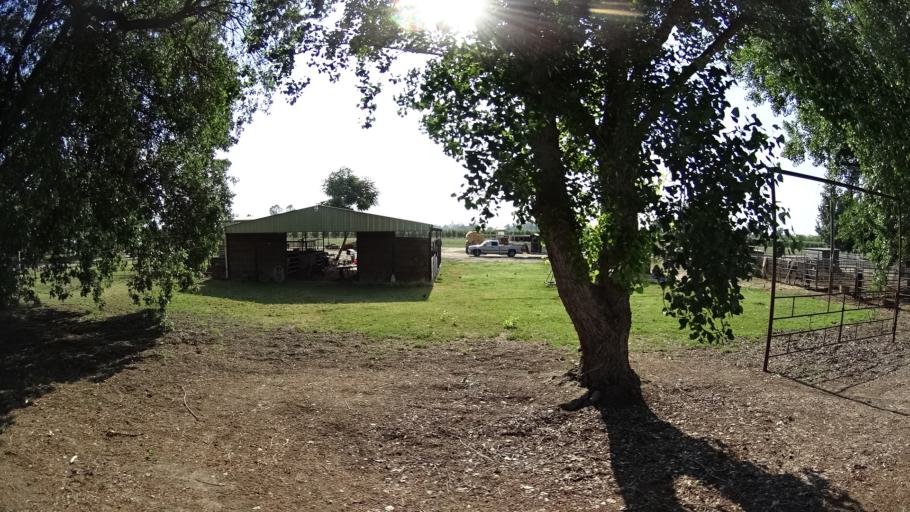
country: US
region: California
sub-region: Kings County
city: Lemoore
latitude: 36.3614
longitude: -119.8250
